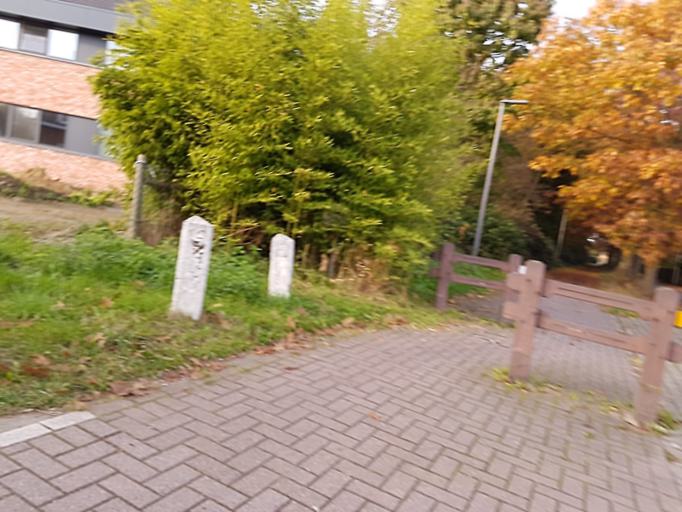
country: BE
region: Flanders
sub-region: Provincie Antwerpen
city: Ranst
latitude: 51.1813
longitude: 4.5907
